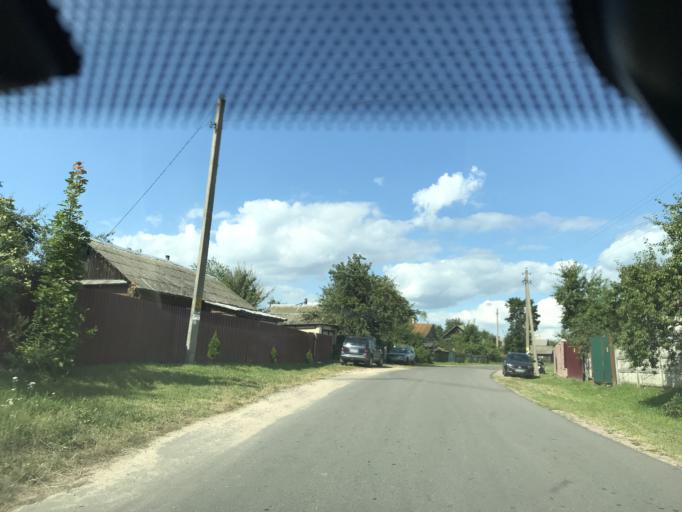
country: BY
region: Mogilev
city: Poselok Voskhod
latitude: 53.7826
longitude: 30.3492
